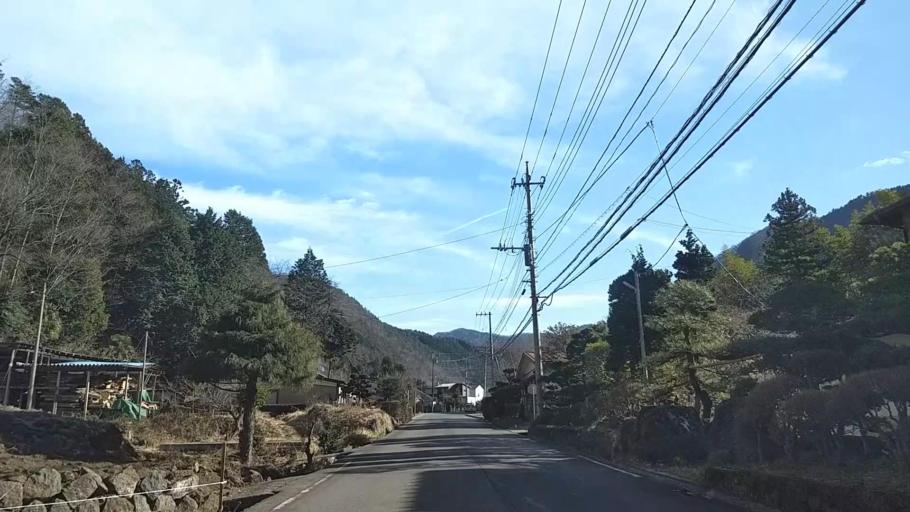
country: JP
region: Yamanashi
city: Otsuki
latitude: 35.5315
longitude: 138.9154
